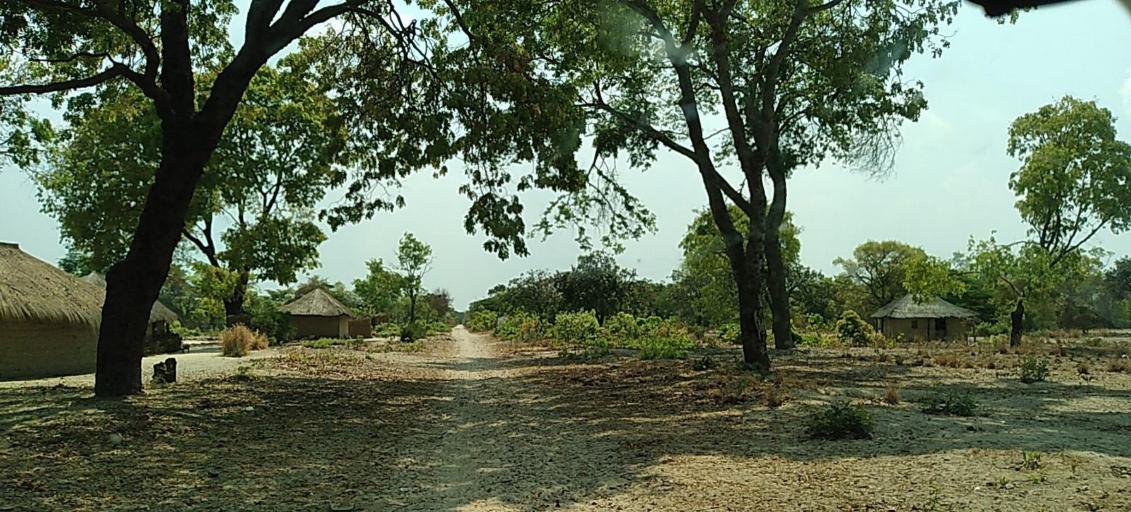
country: ZM
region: North-Western
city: Kabompo
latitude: -13.4013
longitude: 23.8178
